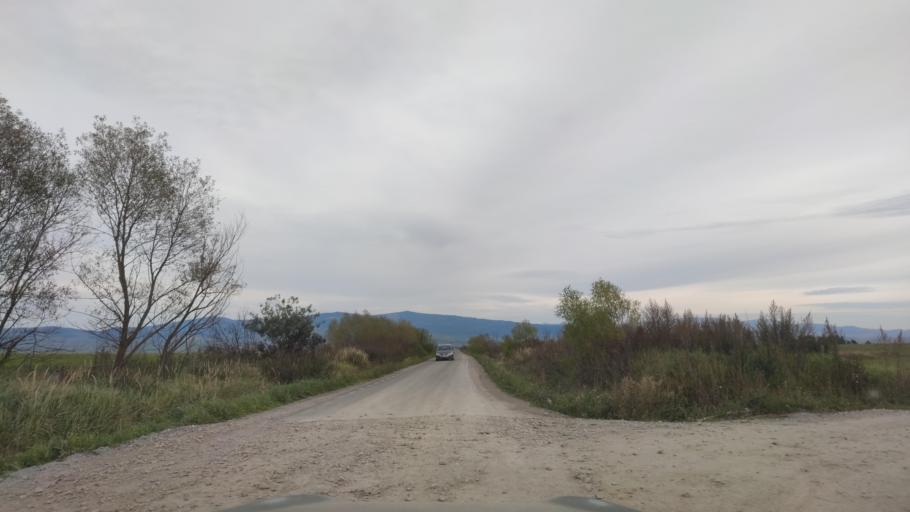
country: RO
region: Harghita
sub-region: Comuna Remetea
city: Remetea
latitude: 46.8081
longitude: 25.4073
